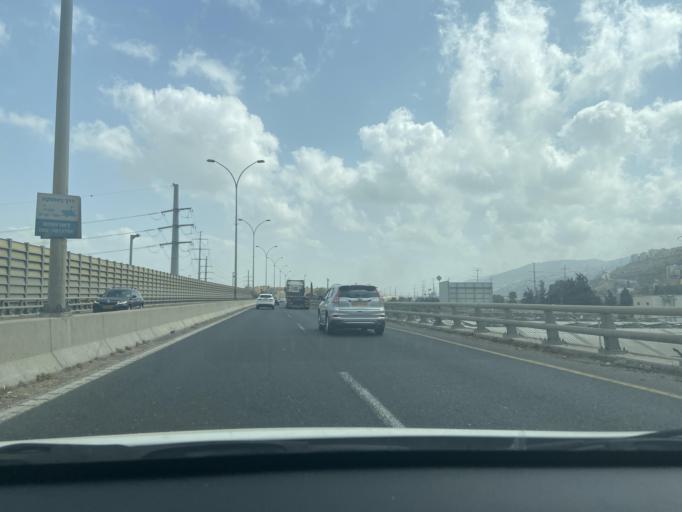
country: IL
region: Haifa
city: Haifa
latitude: 32.8014
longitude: 35.0209
